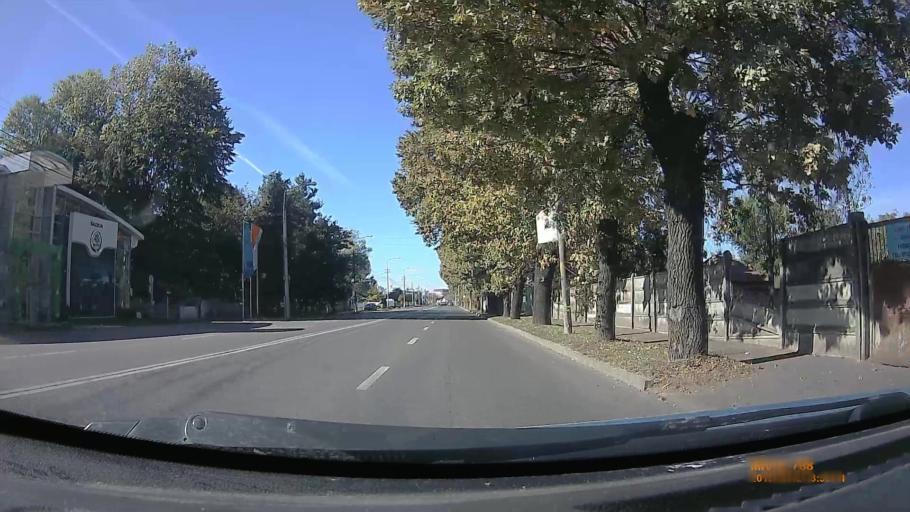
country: RO
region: Bihor
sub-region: Comuna Sanmartin
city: Sanmartin
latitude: 47.0416
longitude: 21.9752
